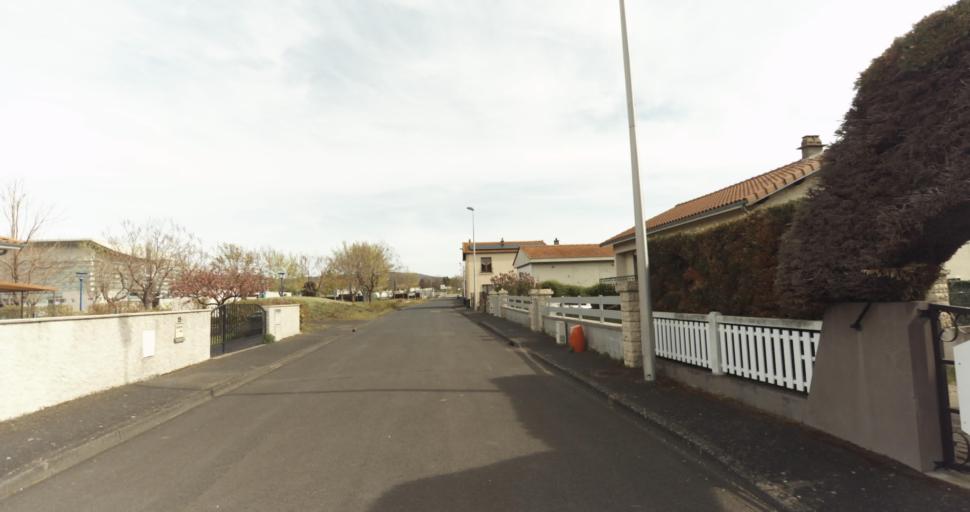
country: FR
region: Auvergne
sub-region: Departement du Puy-de-Dome
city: Cebazat
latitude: 45.8330
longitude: 3.0947
